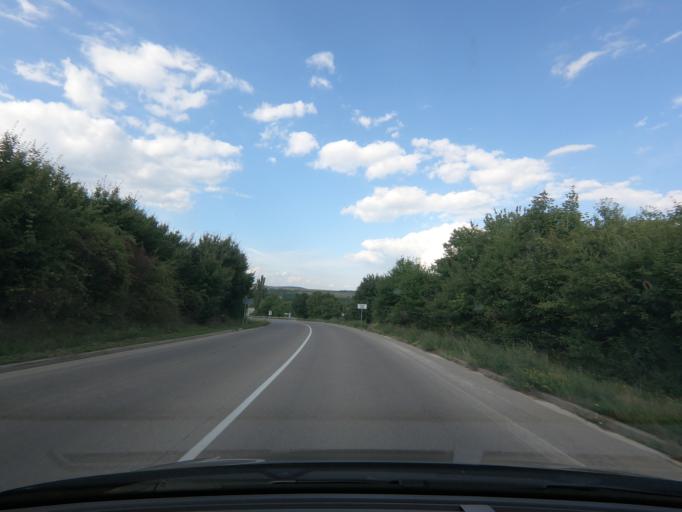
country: SK
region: Nitriansky
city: Stara Tura
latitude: 48.7668
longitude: 17.6942
